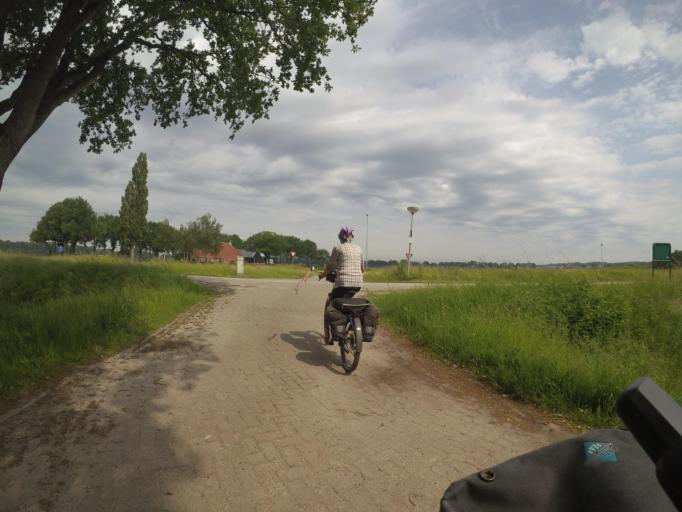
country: NL
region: Drenthe
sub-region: Gemeente Assen
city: Assen
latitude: 53.0143
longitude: 6.4353
